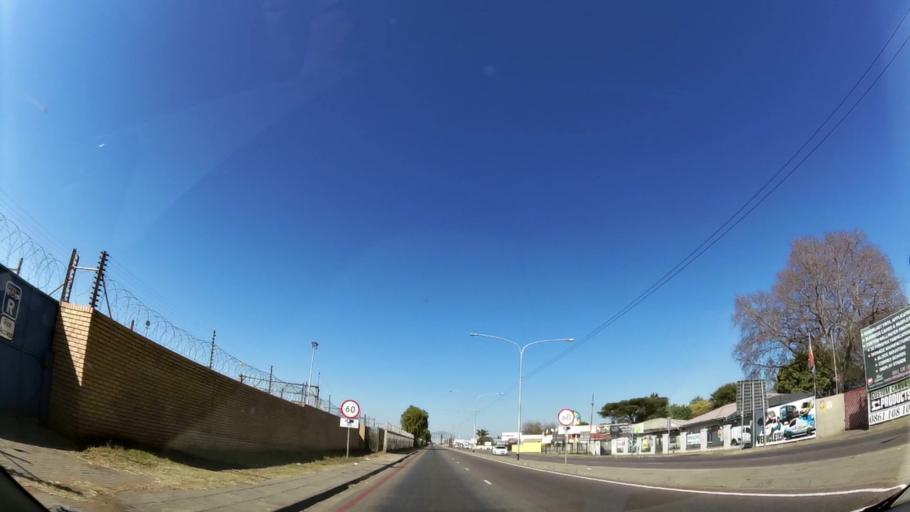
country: ZA
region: Gauteng
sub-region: City of Tshwane Metropolitan Municipality
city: Centurion
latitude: -25.8294
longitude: 28.2075
